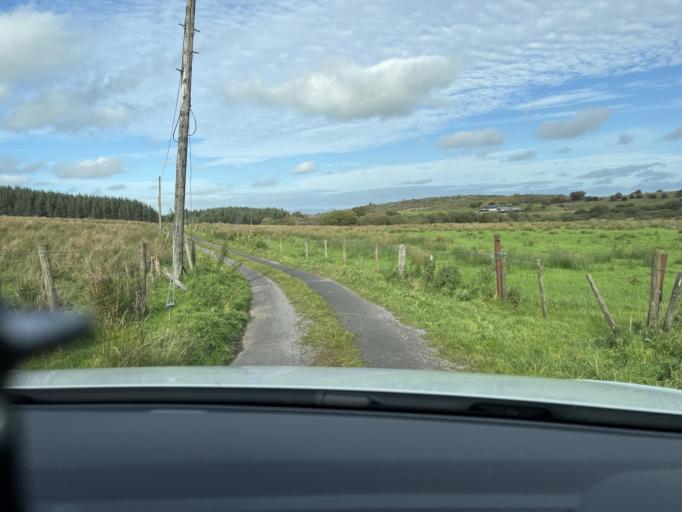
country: IE
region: Connaught
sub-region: Sligo
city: Ballymote
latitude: 54.0653
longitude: -8.4260
